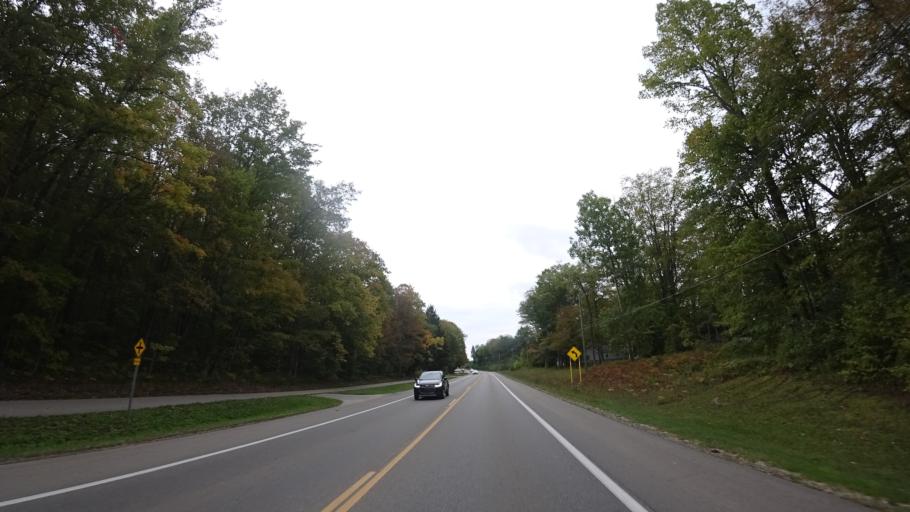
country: US
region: Michigan
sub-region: Emmet County
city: Petoskey
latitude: 45.4286
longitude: -84.9208
